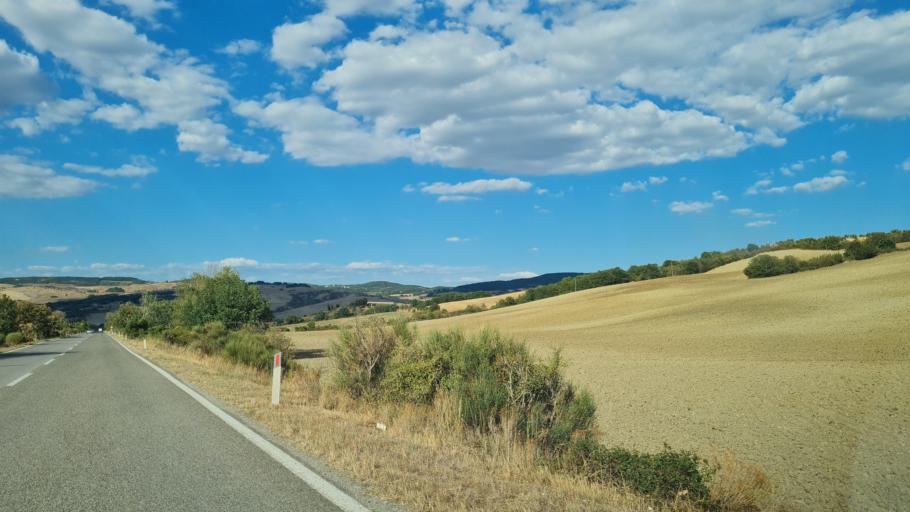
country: IT
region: Tuscany
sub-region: Provincia di Siena
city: Pienza
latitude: 42.9968
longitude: 11.7247
